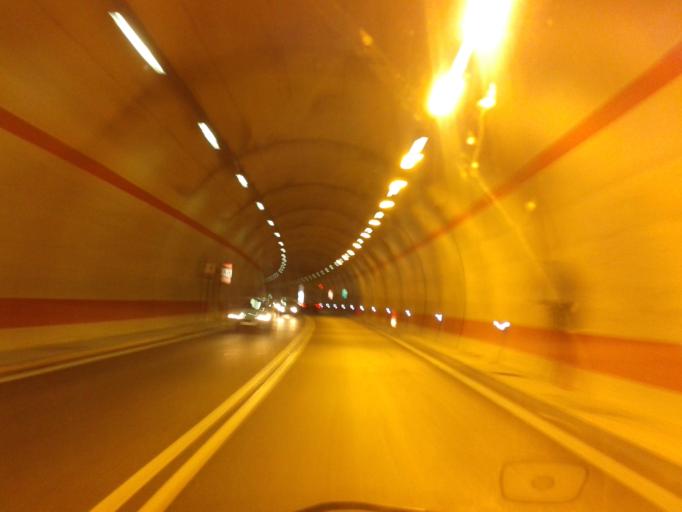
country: IT
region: Sardinia
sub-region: Provincia di Cagliari
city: Quartu Sant'Elena
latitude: 39.1839
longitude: 9.3762
